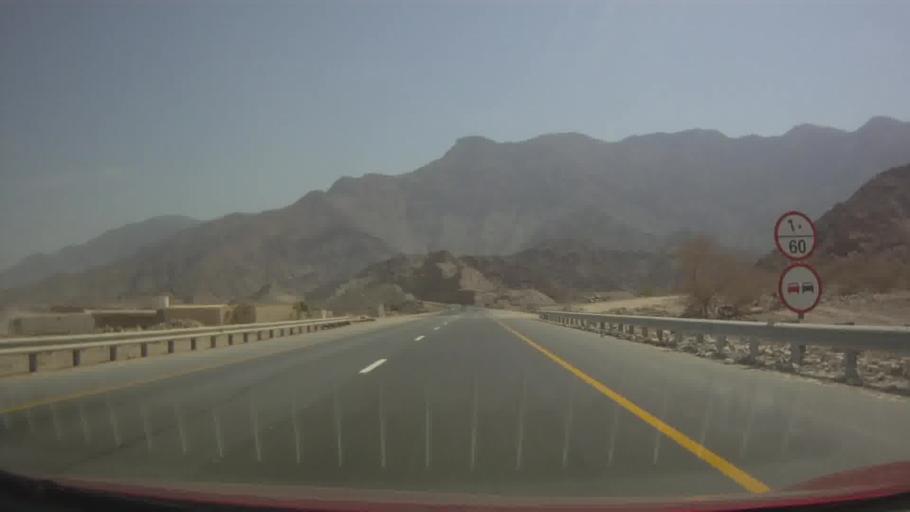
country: OM
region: Muhafazat Masqat
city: Muscat
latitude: 23.4033
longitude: 58.7810
